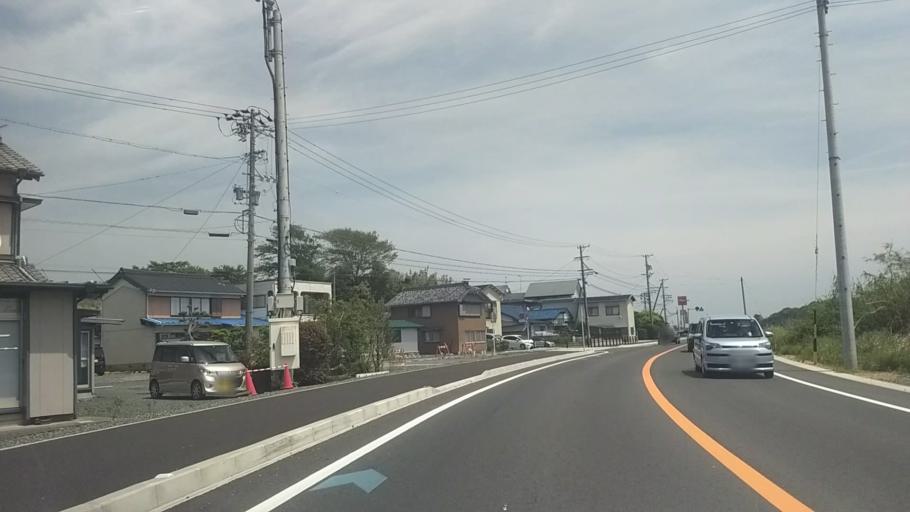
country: JP
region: Shizuoka
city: Kosai-shi
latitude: 34.7597
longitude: 137.5133
